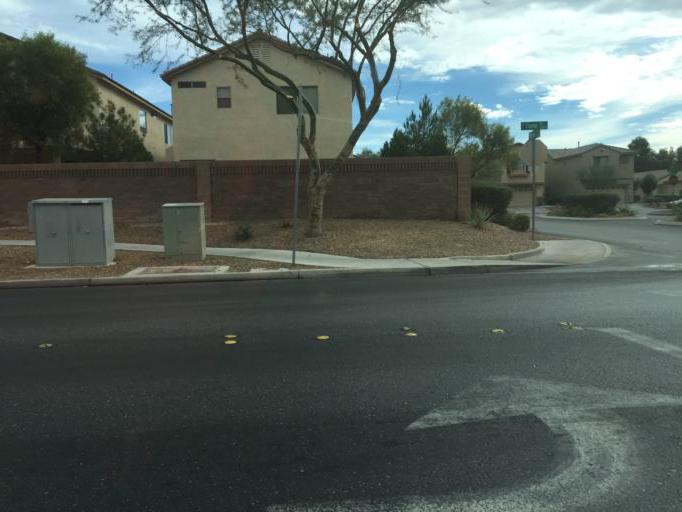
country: US
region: Nevada
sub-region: Clark County
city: Whitney
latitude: 36.1225
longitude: -115.0354
